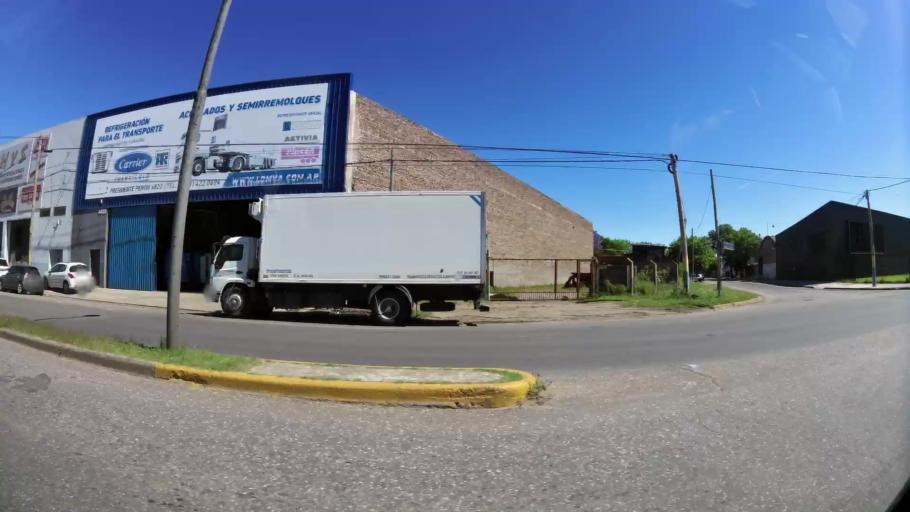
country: AR
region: Santa Fe
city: Perez
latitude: -32.9687
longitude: -60.7128
